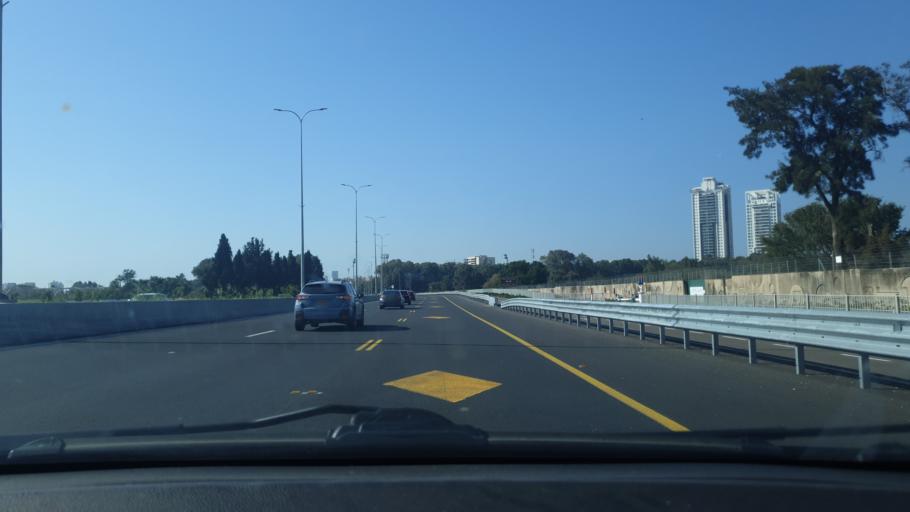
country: IL
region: Tel Aviv
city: Azor
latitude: 32.0414
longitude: 34.8216
